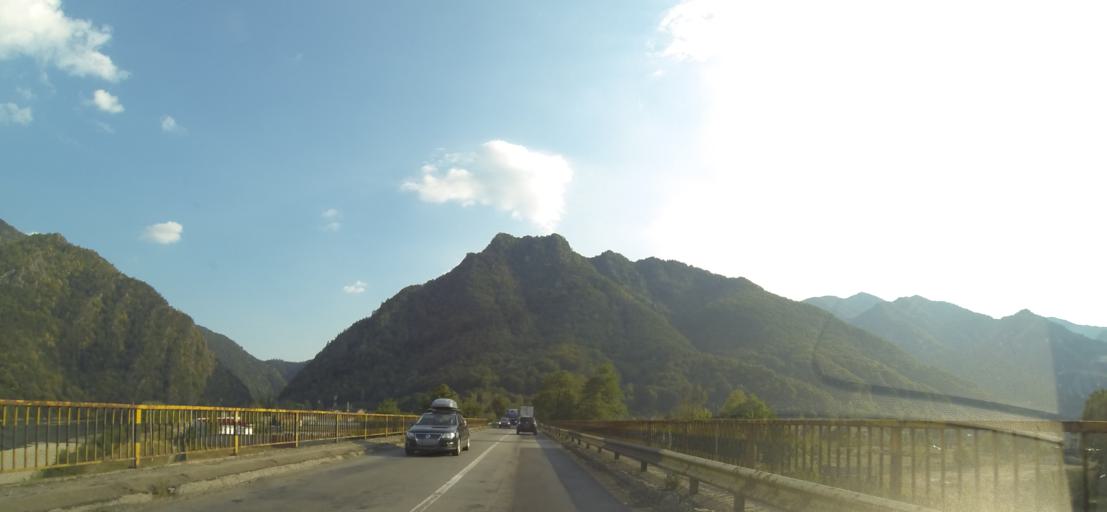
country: RO
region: Valcea
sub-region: Comuna Brezoi
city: Brezoi
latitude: 45.3367
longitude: 24.2743
